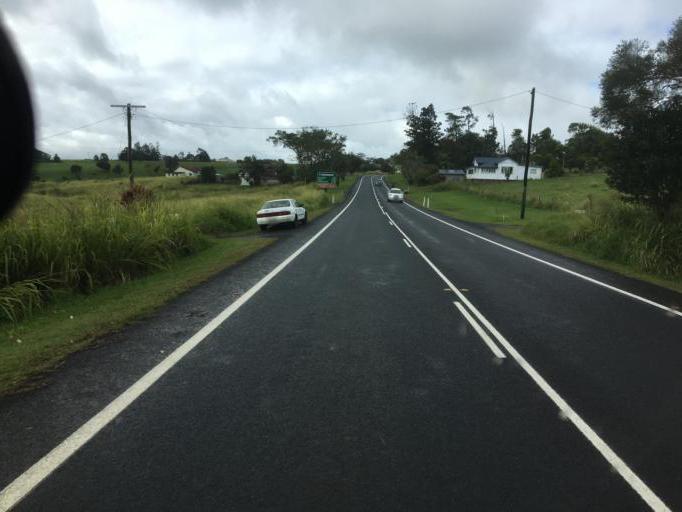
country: AU
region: Queensland
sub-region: Tablelands
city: Ravenshoe
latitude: -17.5115
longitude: 145.6154
